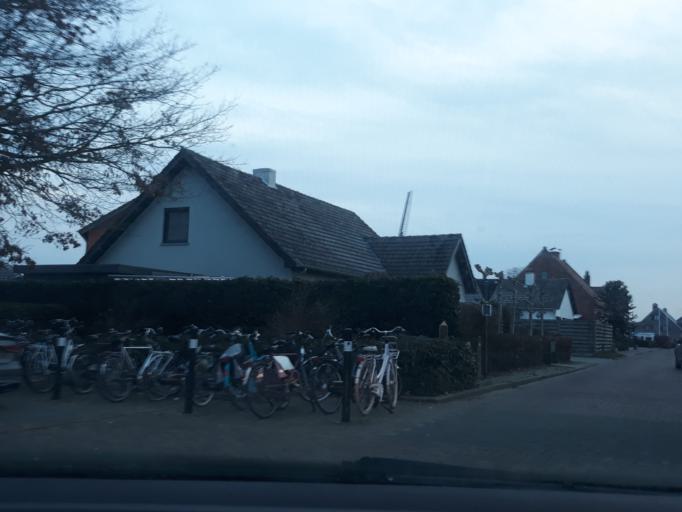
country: BE
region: Flanders
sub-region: Provincie Antwerpen
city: Ravels
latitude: 51.4070
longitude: 4.9906
